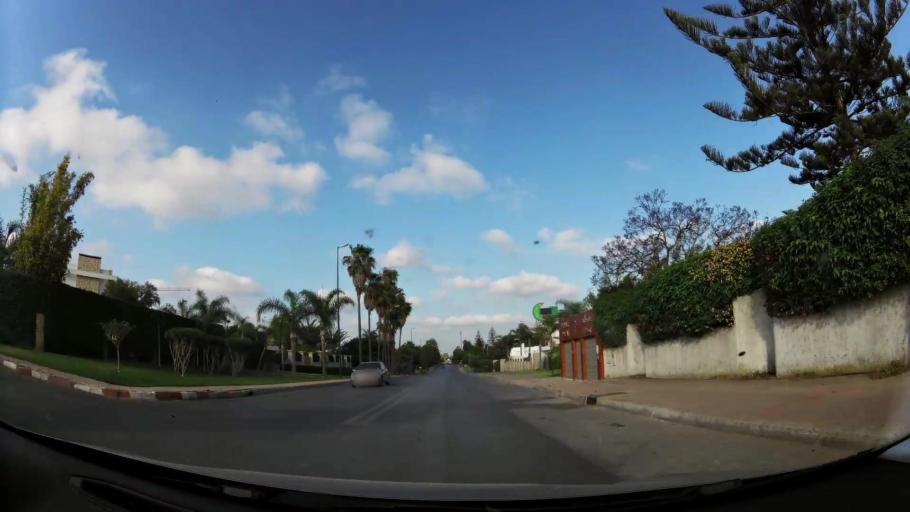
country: MA
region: Rabat-Sale-Zemmour-Zaer
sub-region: Rabat
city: Rabat
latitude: 33.9580
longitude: -6.8485
